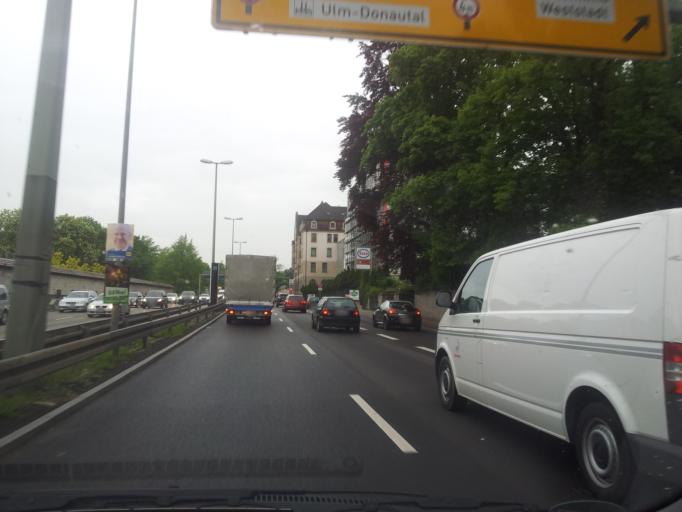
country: DE
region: Baden-Wuerttemberg
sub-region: Tuebingen Region
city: Ulm
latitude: 48.3995
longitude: 9.9773
